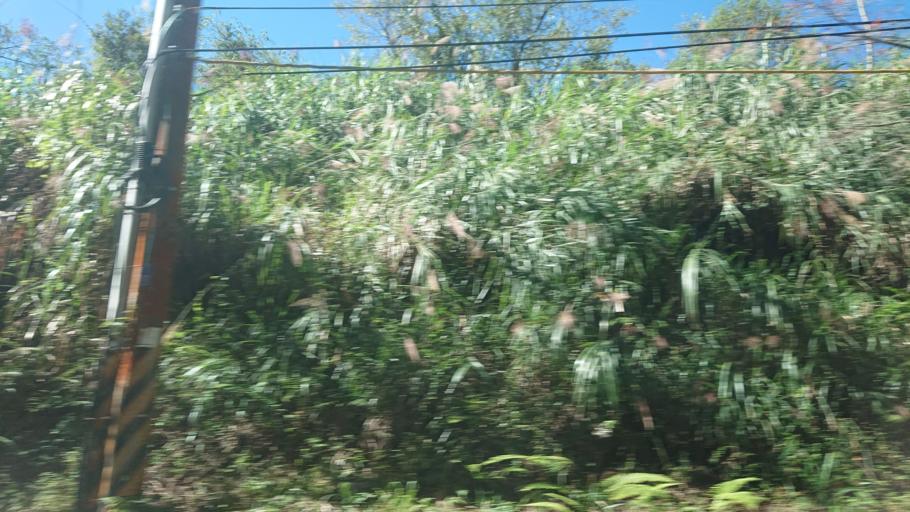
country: TW
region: Taiwan
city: Lugu
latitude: 23.4991
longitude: 120.7951
